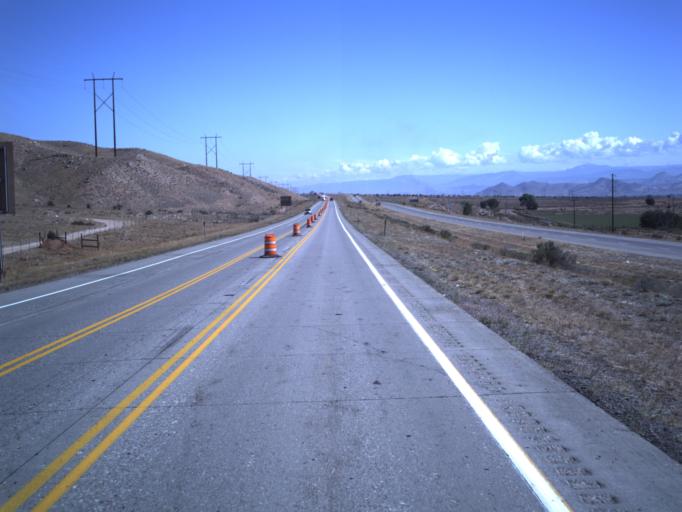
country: US
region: Utah
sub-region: Sevier County
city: Richfield
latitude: 38.7965
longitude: -112.0736
